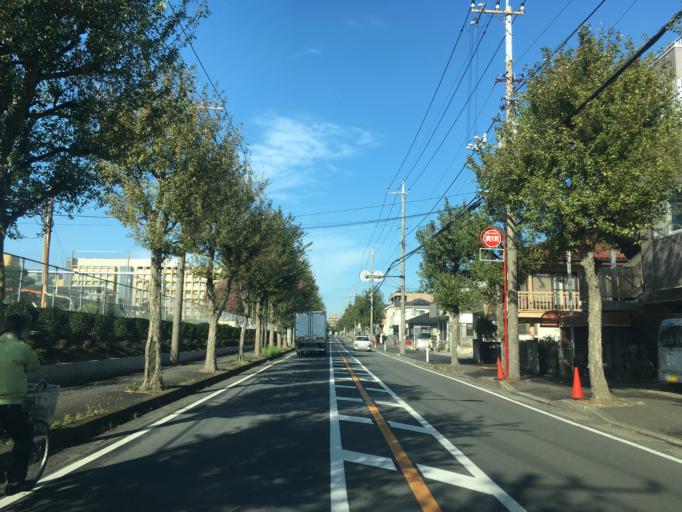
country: JP
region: Tokyo
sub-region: Machida-shi
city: Machida
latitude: 35.5653
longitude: 139.4074
